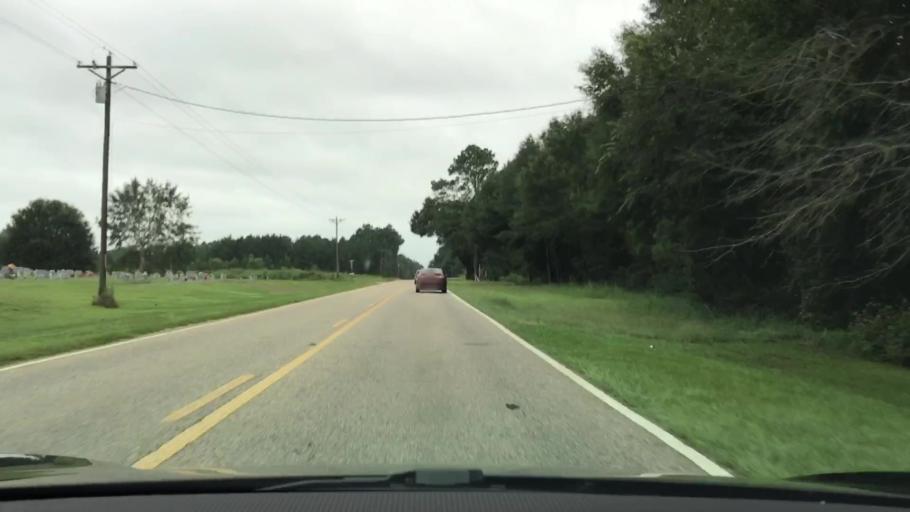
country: US
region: Alabama
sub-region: Geneva County
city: Samson
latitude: 31.1663
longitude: -86.1426
